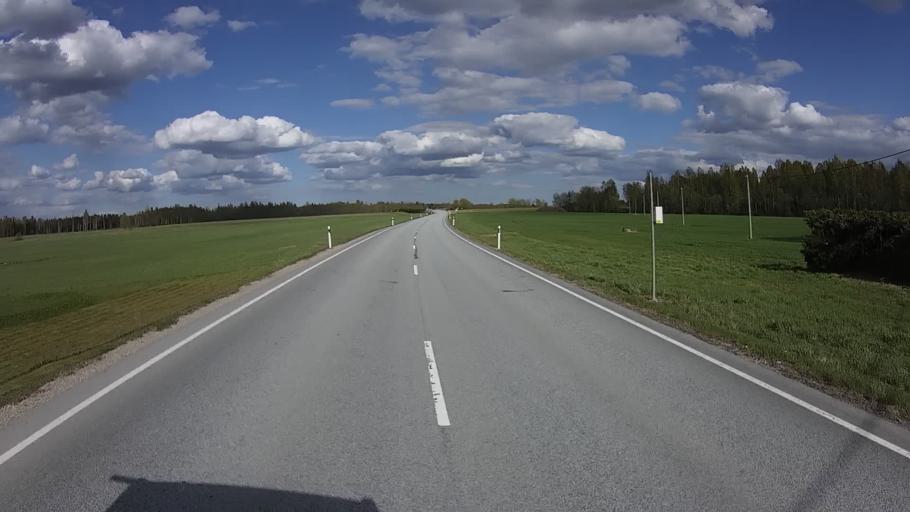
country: EE
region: Jogevamaa
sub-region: Jogeva linn
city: Jogeva
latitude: 58.8156
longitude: 26.5523
